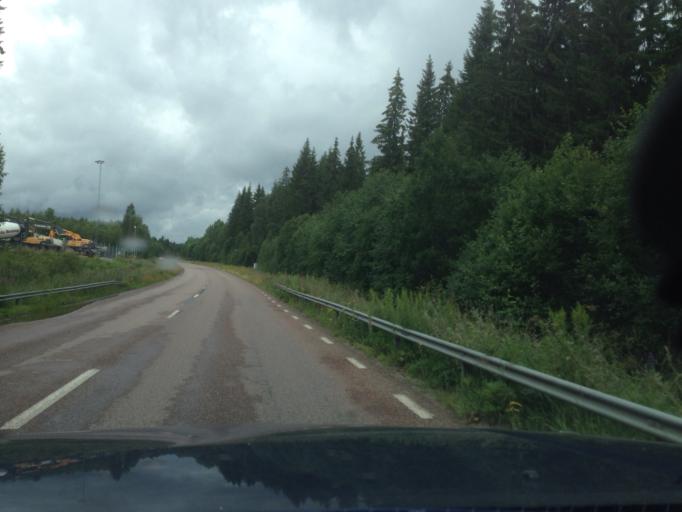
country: SE
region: Dalarna
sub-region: Ludvika Kommun
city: Ludvika
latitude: 60.1403
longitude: 15.1321
